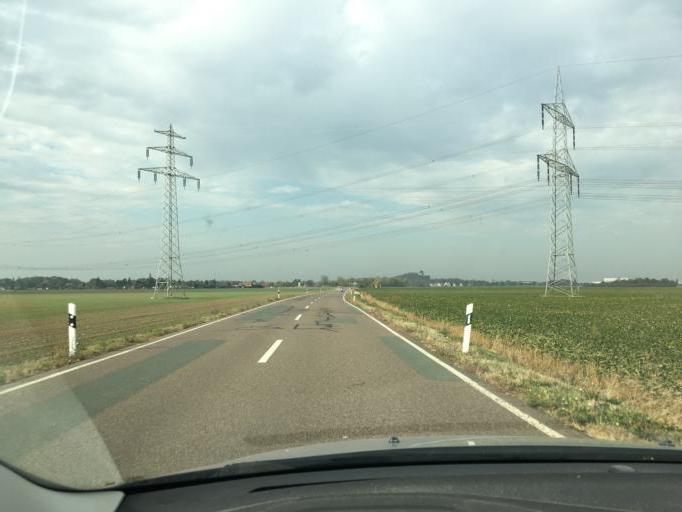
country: DE
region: Saxony-Anhalt
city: Landsberg
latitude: 51.5093
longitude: 12.1851
